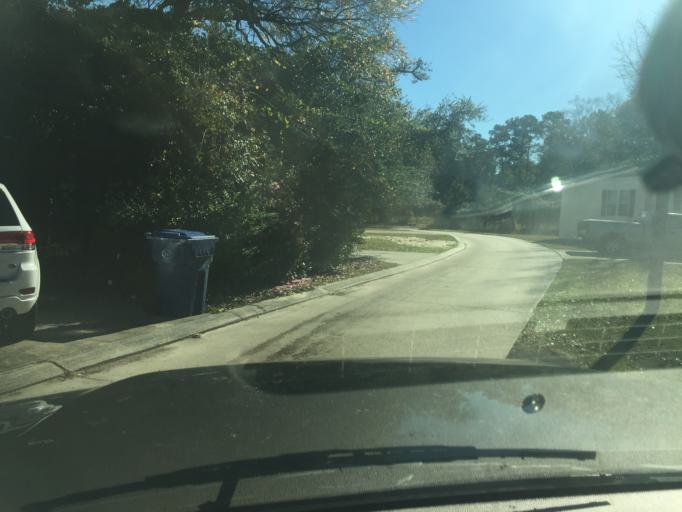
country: US
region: Louisiana
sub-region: Saint Tammany Parish
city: Slidell
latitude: 30.3078
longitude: -89.7312
